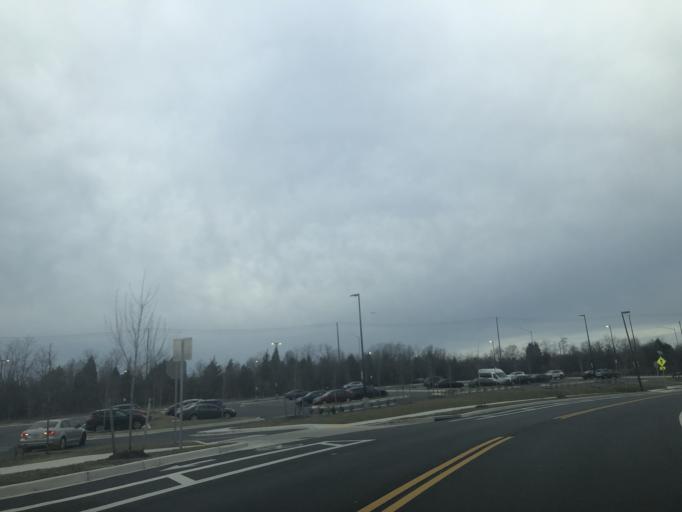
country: US
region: Maryland
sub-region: Prince George's County
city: Oxon Hill
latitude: 38.7998
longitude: -76.9952
